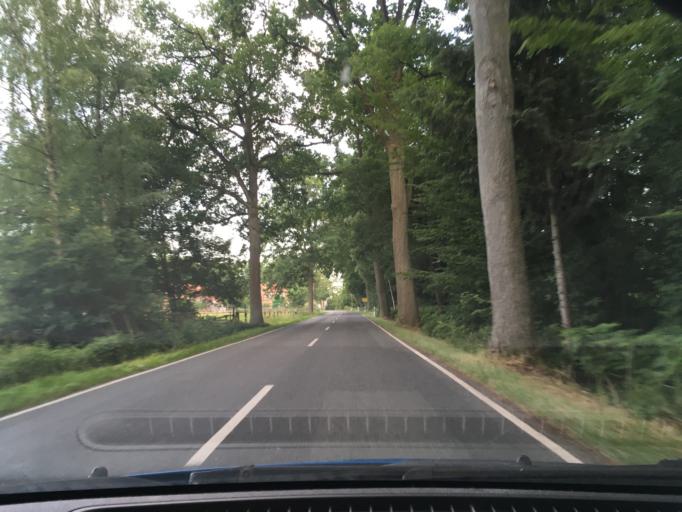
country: DE
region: Lower Saxony
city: Eldingen
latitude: 52.7044
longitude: 10.3197
